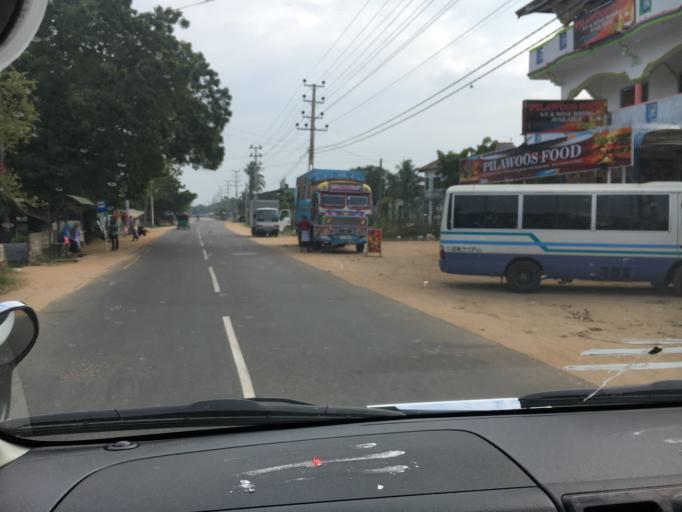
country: LK
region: Eastern Province
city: Trincomalee
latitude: 8.4994
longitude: 81.1918
